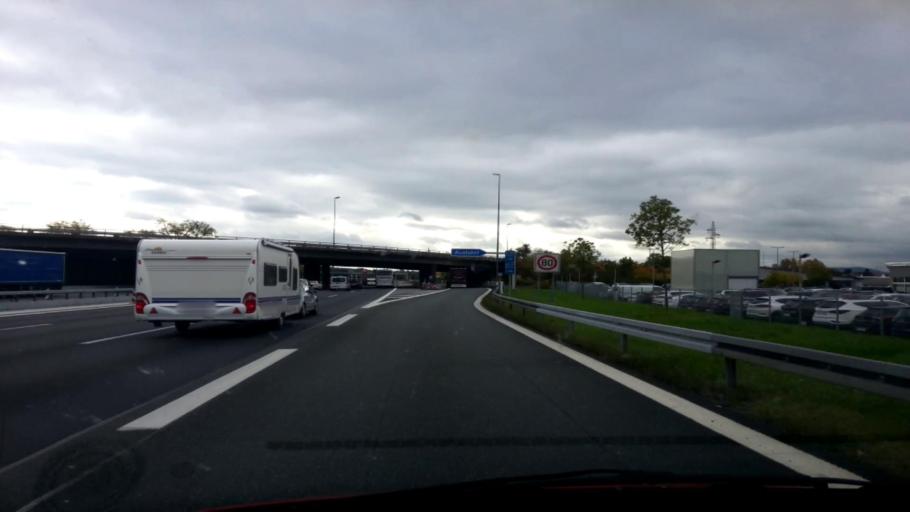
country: DE
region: Bavaria
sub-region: Upper Franconia
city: Bindlach
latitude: 49.9608
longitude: 11.6055
